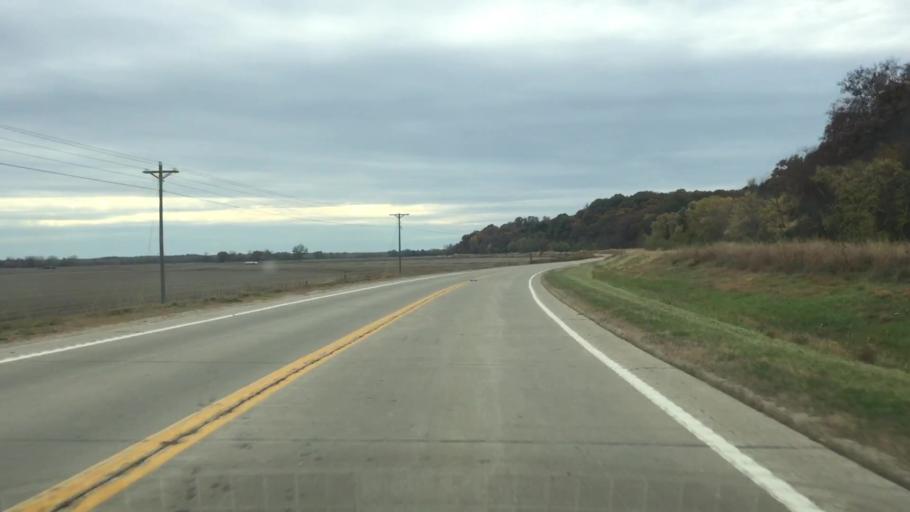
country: US
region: Missouri
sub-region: Callaway County
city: Holts Summit
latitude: 38.5872
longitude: -92.0326
